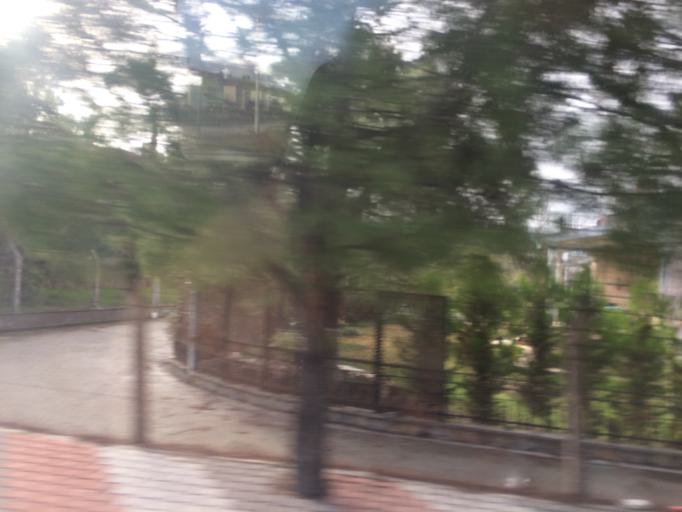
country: TR
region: Izmir
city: Menemen
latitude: 38.5045
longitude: 26.9589
